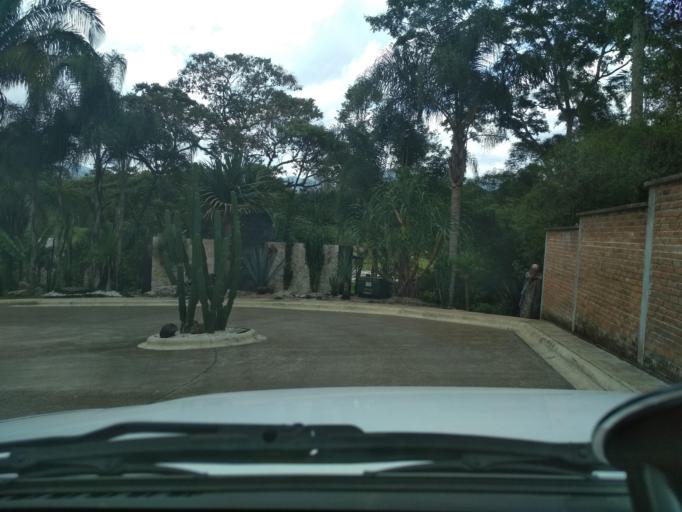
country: MX
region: Veracruz
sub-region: Cordoba
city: San Jose de Abajo [Unidad Habitacional]
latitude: 18.9183
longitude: -96.9542
